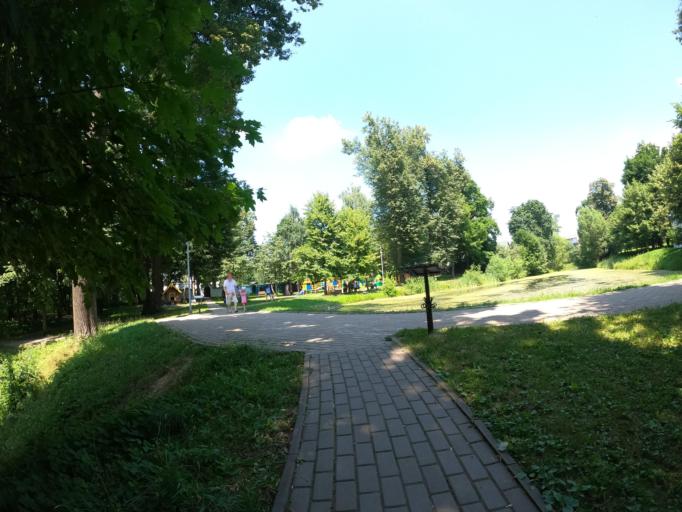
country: RU
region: Kaluga
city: Obninsk
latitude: 55.1253
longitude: 36.5922
